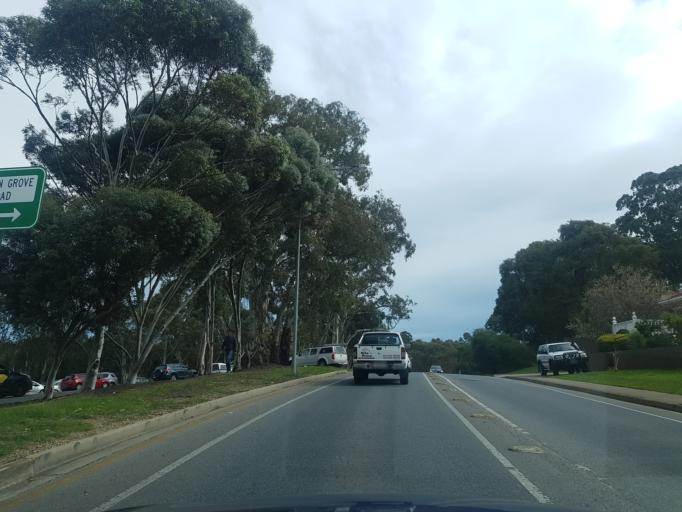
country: AU
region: South Australia
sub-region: Tea Tree Gully
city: Hope Valley
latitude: -34.8171
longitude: 138.6973
